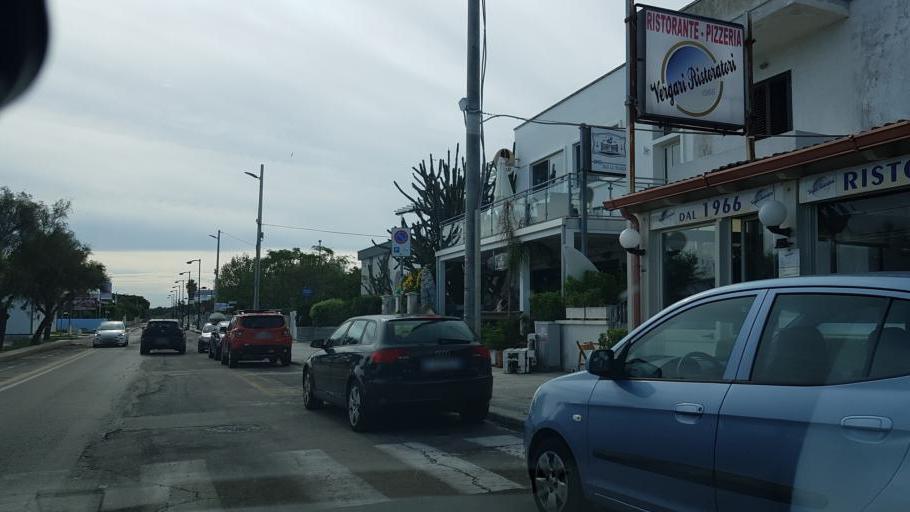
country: IT
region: Apulia
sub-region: Provincia di Lecce
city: Borgagne
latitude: 40.3009
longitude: 18.4058
